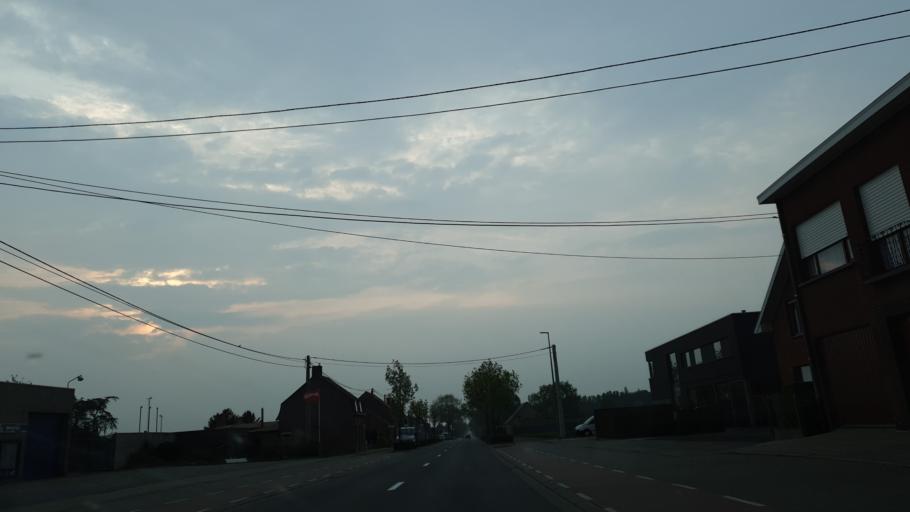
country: BE
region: Flanders
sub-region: Provincie West-Vlaanderen
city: Poperinge
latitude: 50.9038
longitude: 2.7848
